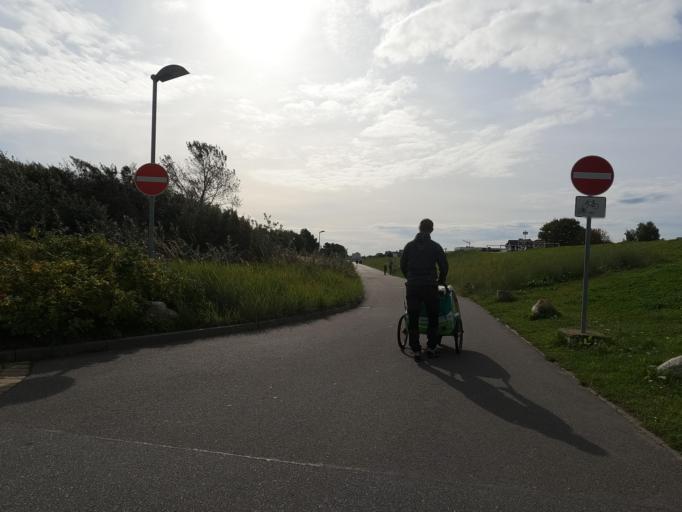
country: DE
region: Schleswig-Holstein
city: Dahme
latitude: 54.2304
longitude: 11.0850
